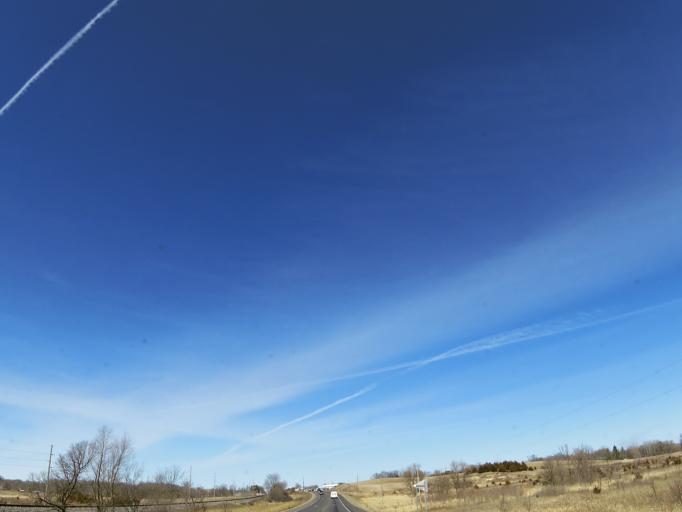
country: US
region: Minnesota
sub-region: Wright County
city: Buffalo
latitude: 45.1318
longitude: -93.8220
